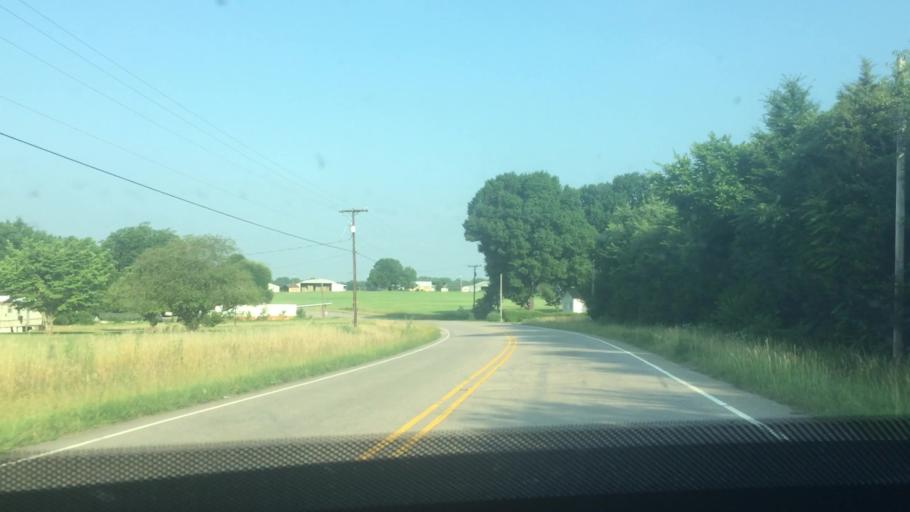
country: US
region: North Carolina
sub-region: Rowan County
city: Enochville
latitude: 35.5818
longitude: -80.7216
